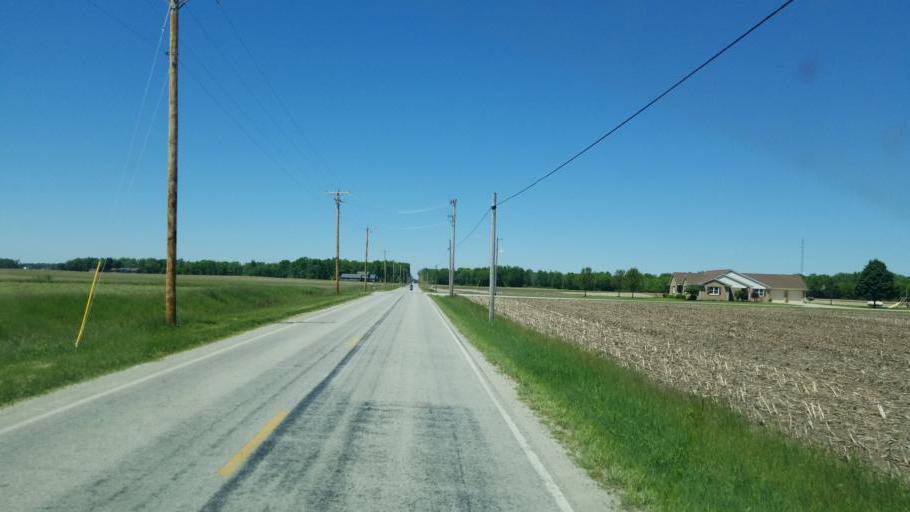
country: US
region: Ohio
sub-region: Shelby County
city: Fort Loramie
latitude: 40.3544
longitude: -84.3339
